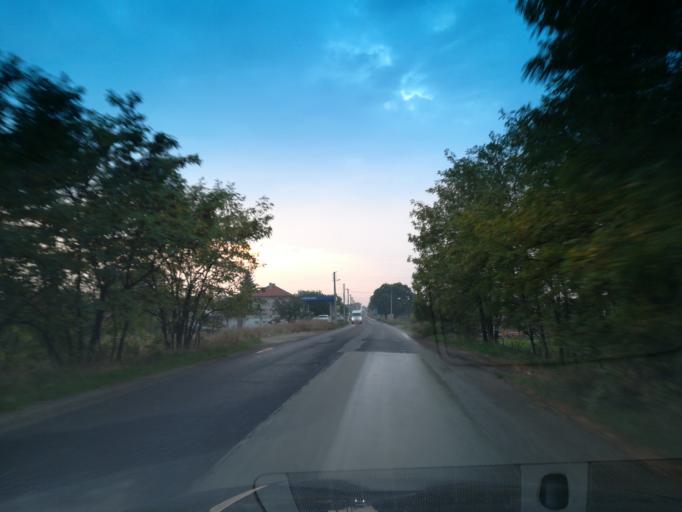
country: BG
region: Stara Zagora
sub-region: Obshtina Chirpan
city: Chirpan
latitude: 42.1778
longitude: 25.2135
